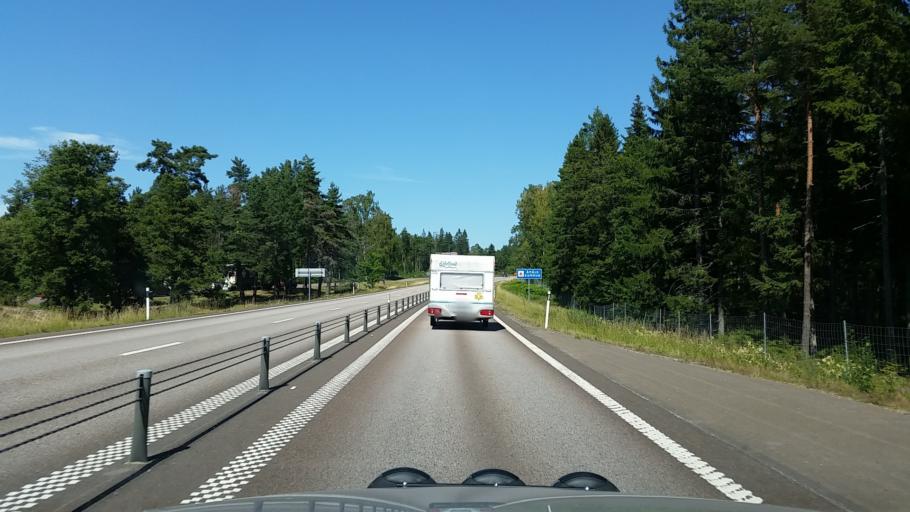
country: SE
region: Vaestra Goetaland
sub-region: Melleruds Kommun
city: Mellerud
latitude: 58.8229
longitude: 12.5242
